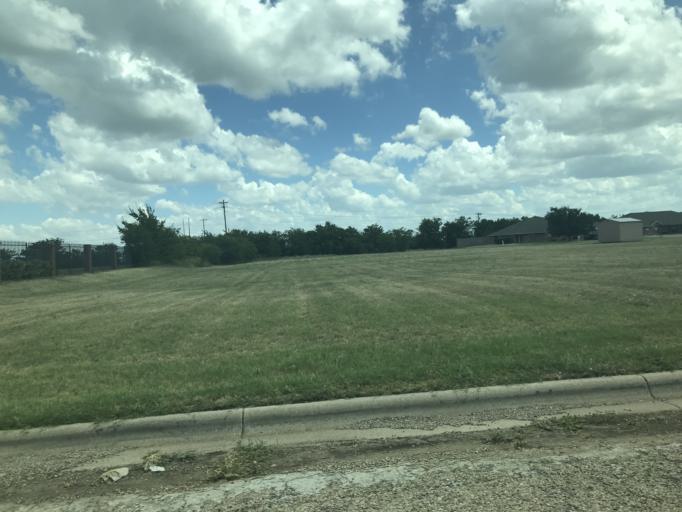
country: US
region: Texas
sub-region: Taylor County
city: Abilene
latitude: 32.4439
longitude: -99.7000
